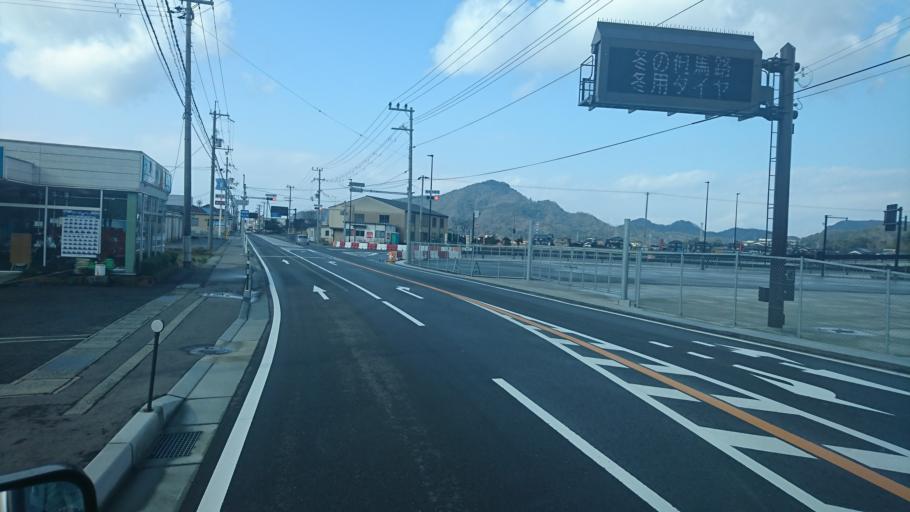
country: JP
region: Tottori
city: Tottori
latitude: 35.6108
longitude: 134.4700
